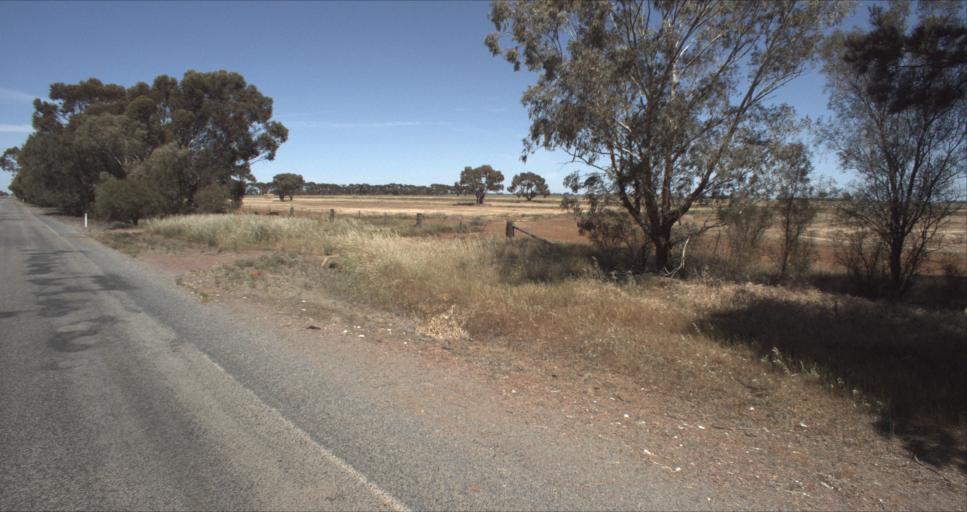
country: AU
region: New South Wales
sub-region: Leeton
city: Leeton
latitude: -34.4678
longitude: 146.2929
